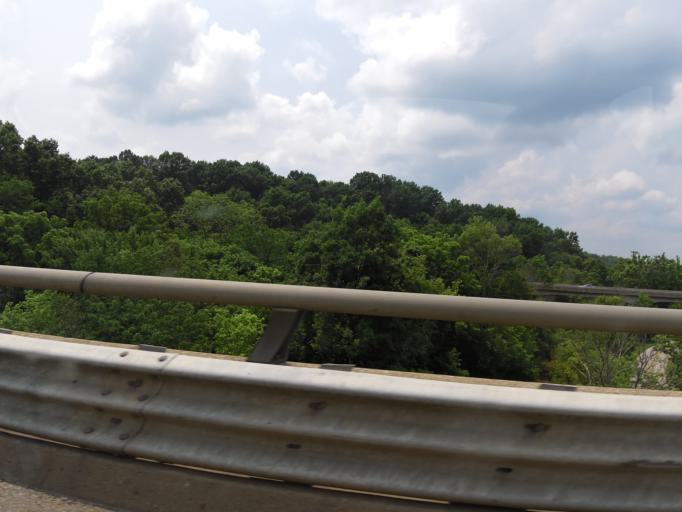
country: US
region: Kentucky
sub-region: Trimble County
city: Providence
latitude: 38.4798
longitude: -85.2688
